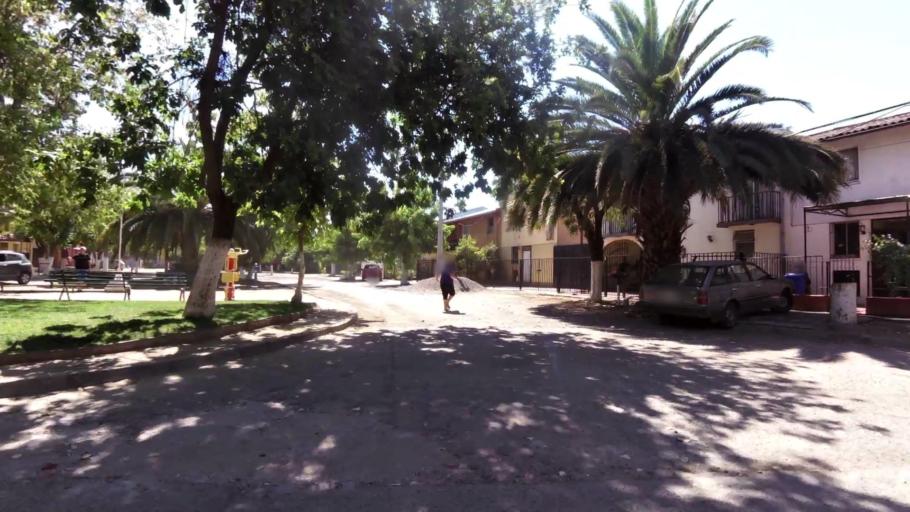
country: CL
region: Maule
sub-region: Provincia de Talca
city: Talca
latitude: -35.4142
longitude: -71.6497
